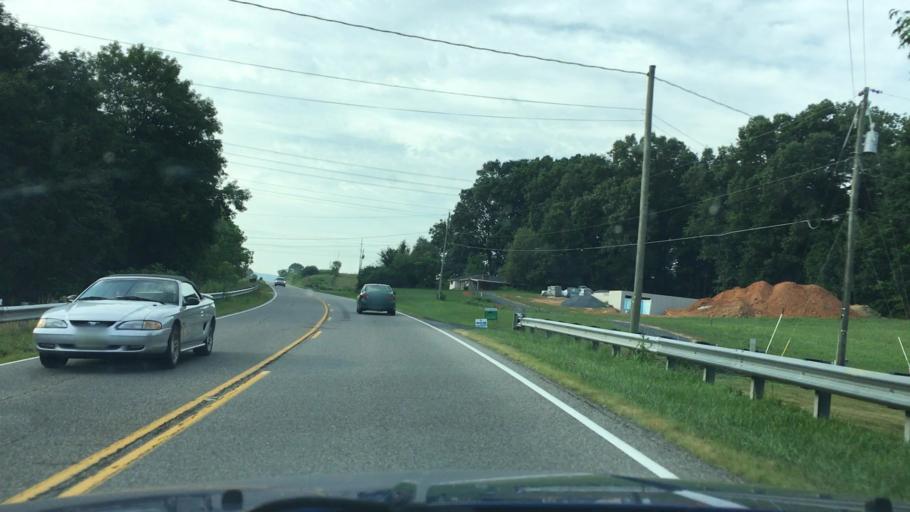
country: US
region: Virginia
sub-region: Augusta County
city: Dooms
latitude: 38.1239
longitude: -78.9143
